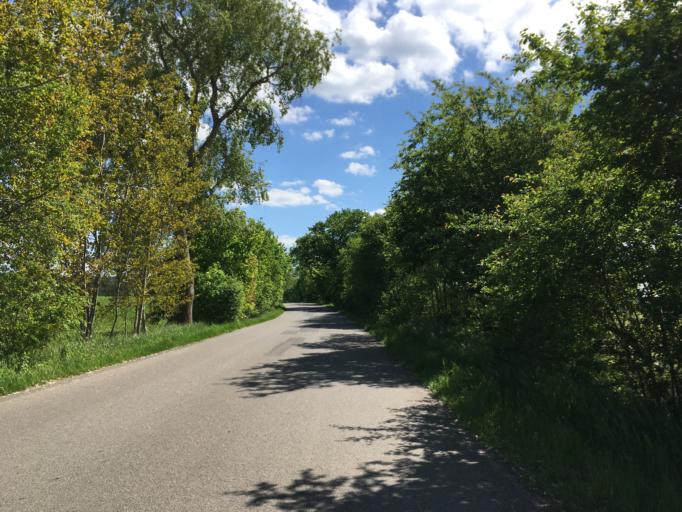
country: DE
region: Brandenburg
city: Rudnitz
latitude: 52.7036
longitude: 13.6627
